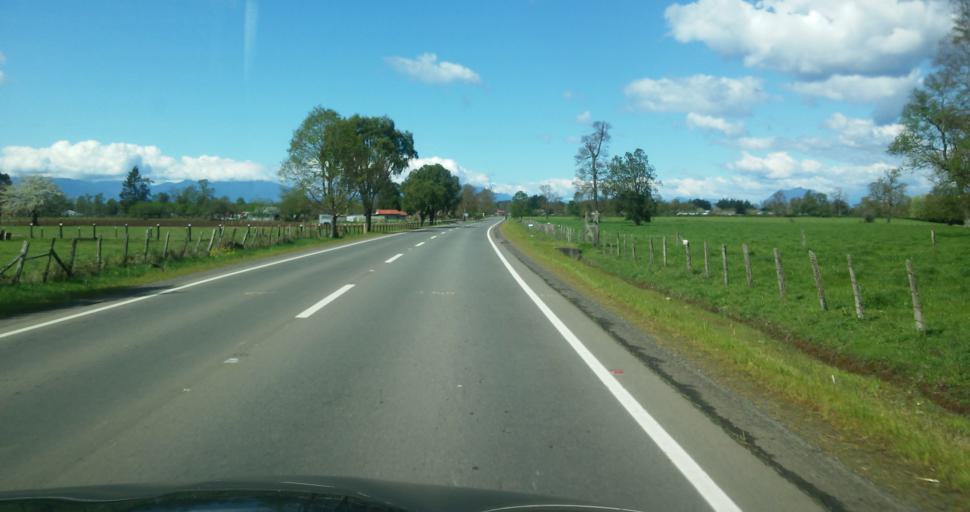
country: CL
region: Los Rios
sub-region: Provincia del Ranco
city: Rio Bueno
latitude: -40.2404
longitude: -72.6040
